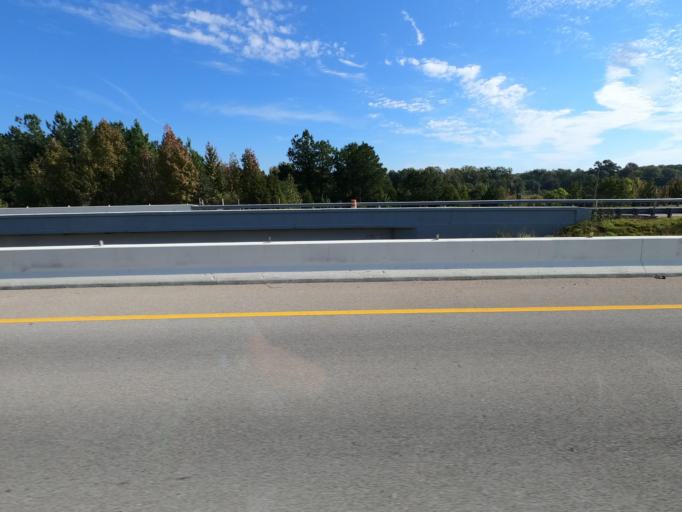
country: US
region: Tennessee
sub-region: Shelby County
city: Arlington
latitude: 35.3041
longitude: -89.6976
